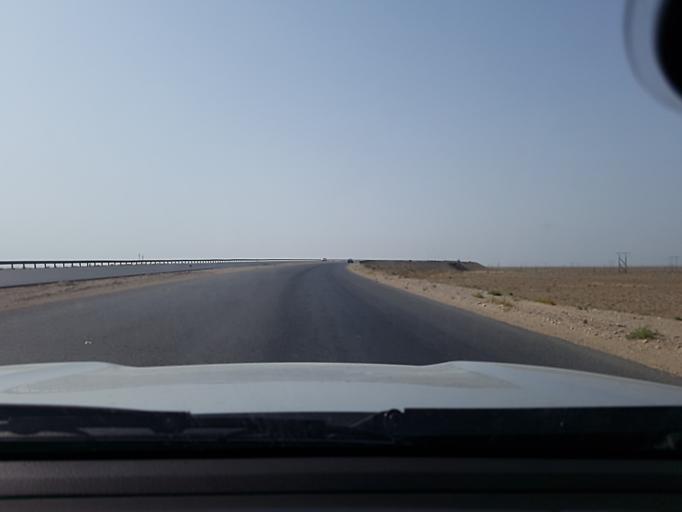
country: TM
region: Balkan
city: Balkanabat
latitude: 39.4454
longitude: 54.4777
